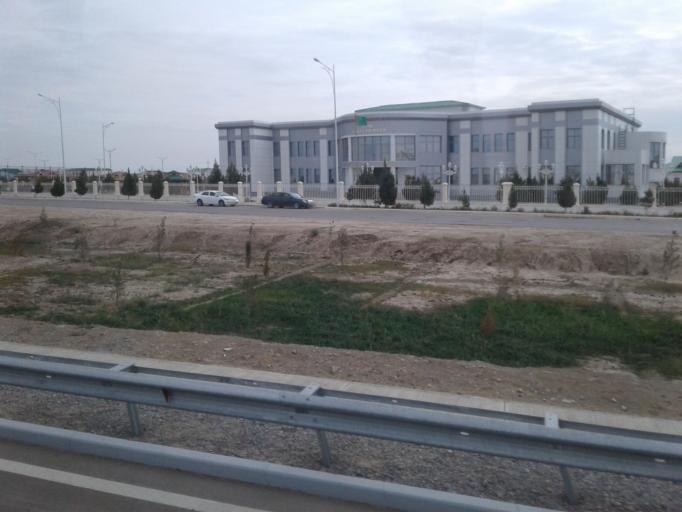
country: TM
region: Lebap
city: Turkmenabat
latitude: 38.9873
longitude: 63.5624
